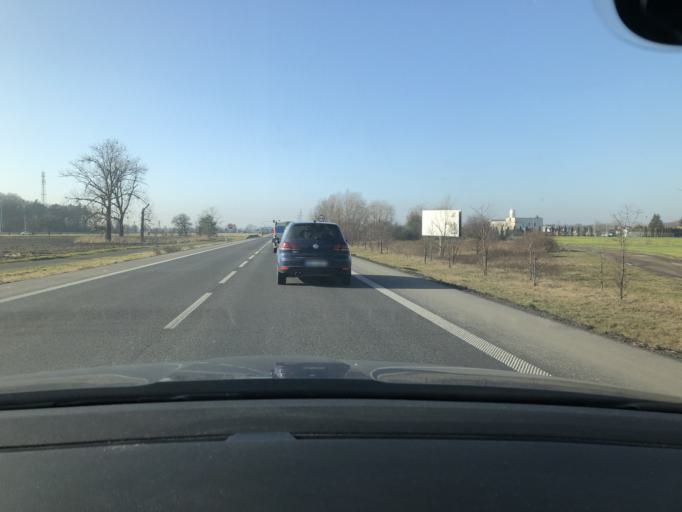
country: PL
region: Greater Poland Voivodeship
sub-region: Powiat szamotulski
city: Pniewy
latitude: 52.4998
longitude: 16.2596
